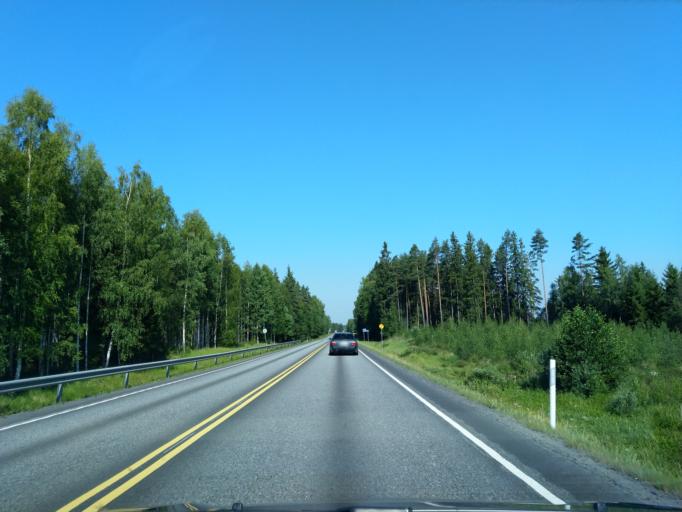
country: FI
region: Satakunta
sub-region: Pori
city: Huittinen
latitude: 61.1404
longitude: 22.7633
